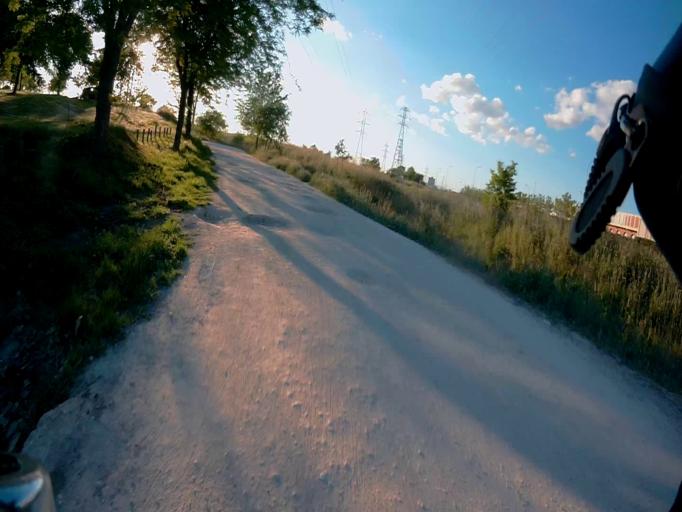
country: ES
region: Madrid
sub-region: Provincia de Madrid
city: Leganes
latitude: 40.3260
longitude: -3.7880
